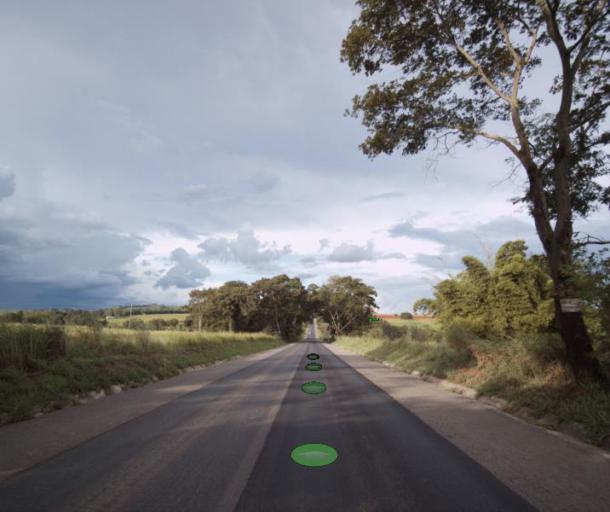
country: BR
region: Goias
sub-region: Itapaci
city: Itapaci
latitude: -15.1163
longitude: -49.4949
